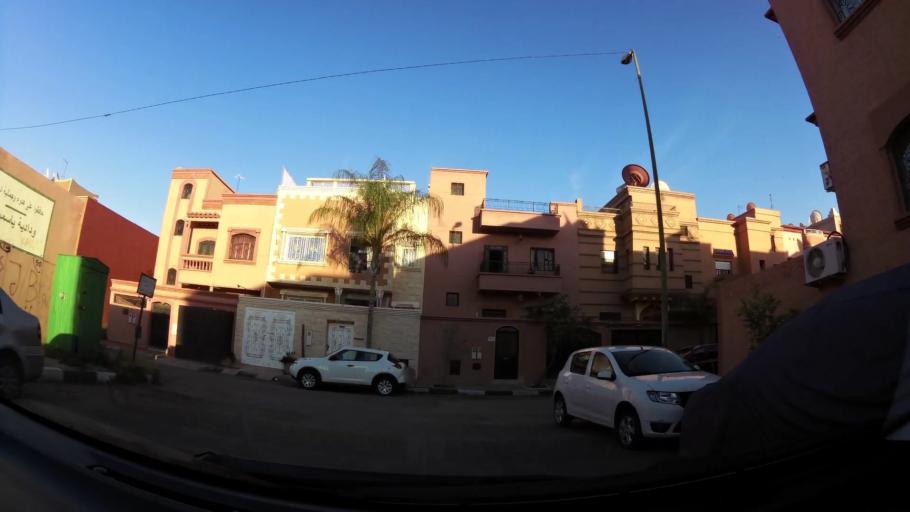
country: MA
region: Marrakech-Tensift-Al Haouz
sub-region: Marrakech
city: Marrakesh
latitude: 31.6238
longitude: -8.0322
